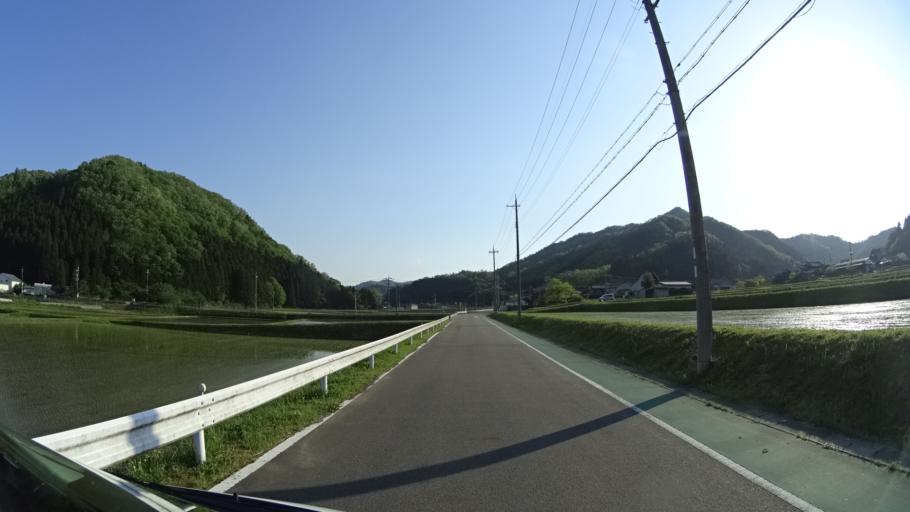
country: JP
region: Kyoto
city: Kameoka
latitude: 35.1422
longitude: 135.4204
